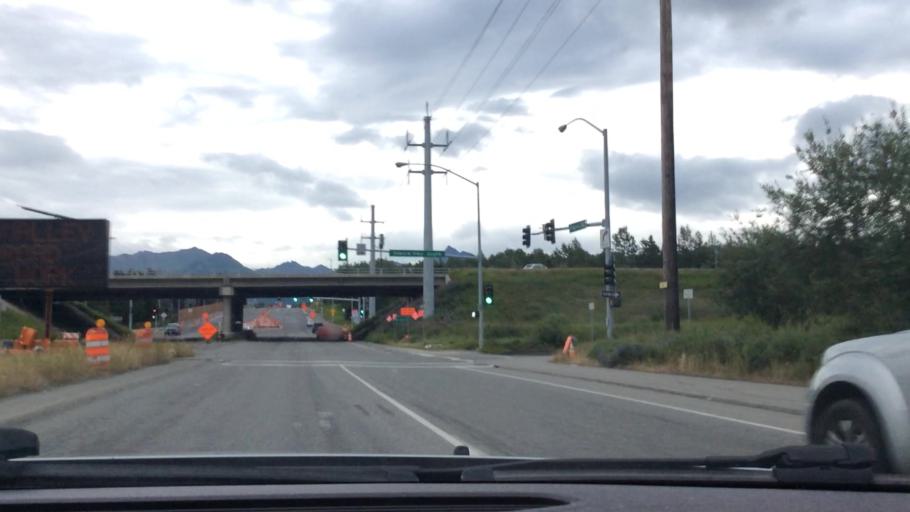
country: US
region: Alaska
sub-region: Anchorage Municipality
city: Anchorage
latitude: 61.1230
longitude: -149.8586
